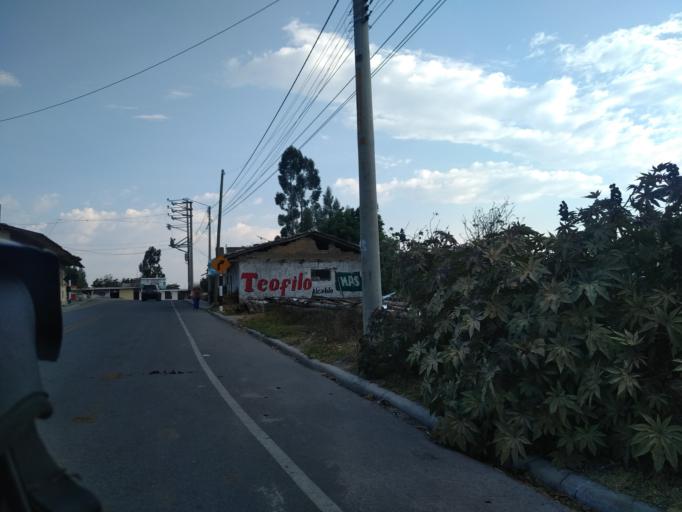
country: PE
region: Cajamarca
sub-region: San Marcos
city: La Grama
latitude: -7.3873
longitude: -78.1241
